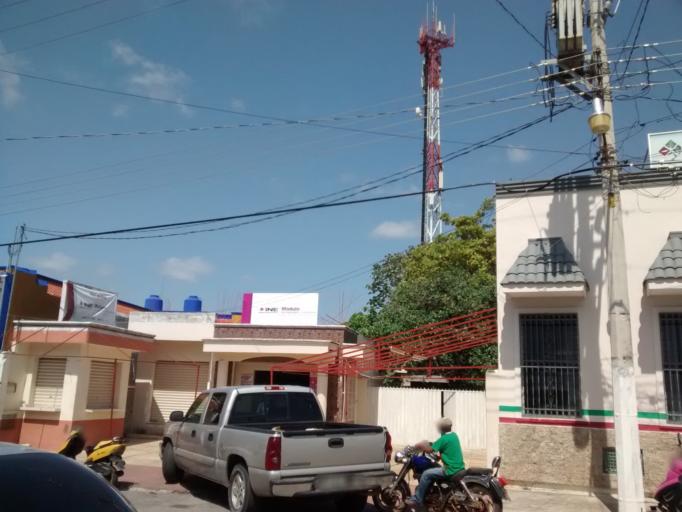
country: MX
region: Yucatan
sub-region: Tizimin
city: Tizimin
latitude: 21.1410
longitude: -88.1517
